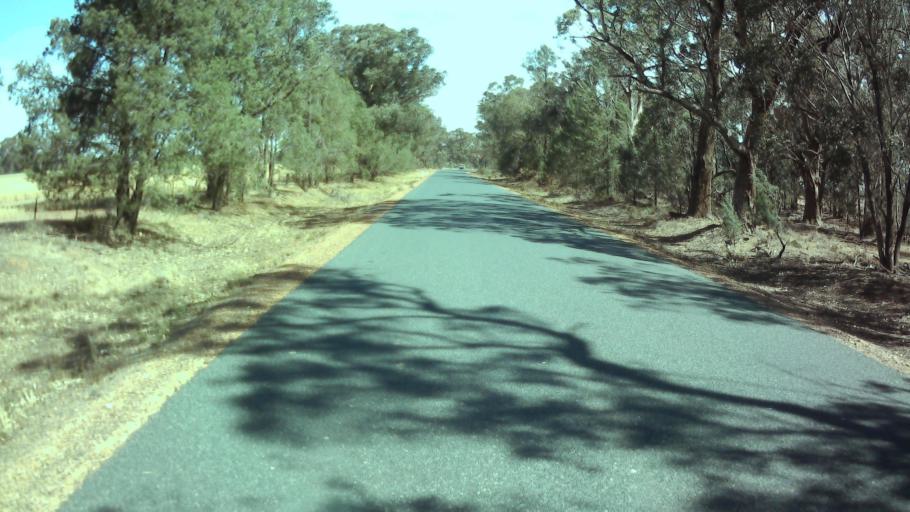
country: AU
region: New South Wales
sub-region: Weddin
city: Grenfell
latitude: -34.0348
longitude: 148.1342
